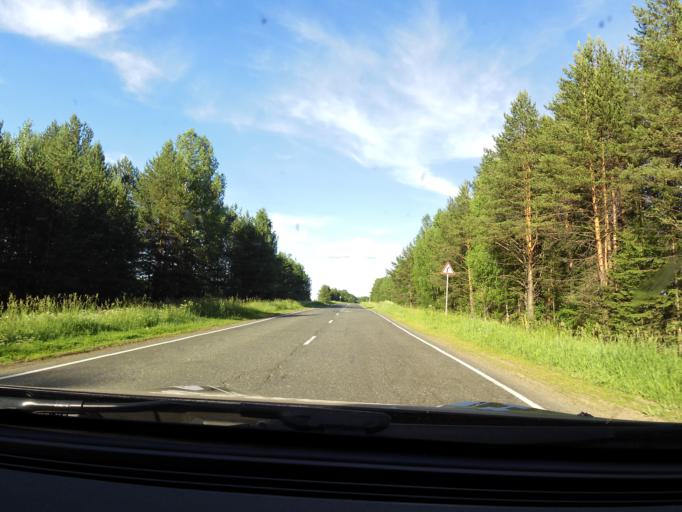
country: RU
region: Kirov
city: Belorechensk
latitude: 58.8074
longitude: 52.4563
